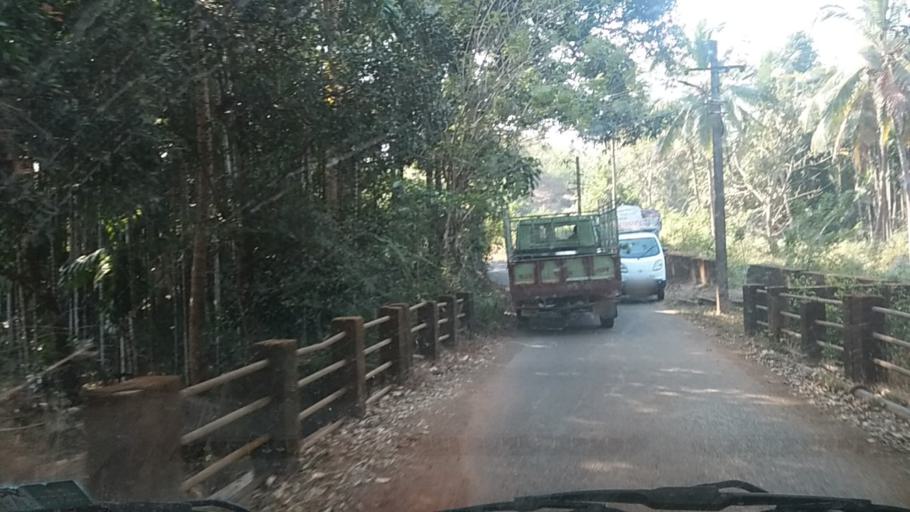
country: IN
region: Goa
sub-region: North Goa
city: Ponda
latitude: 15.4013
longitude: 74.0613
